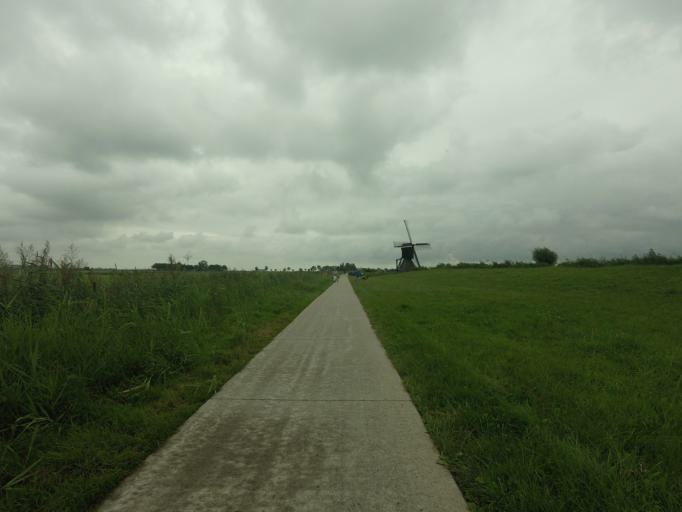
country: NL
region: Friesland
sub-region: Sudwest Fryslan
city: Bolsward
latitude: 52.9985
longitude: 5.5357
